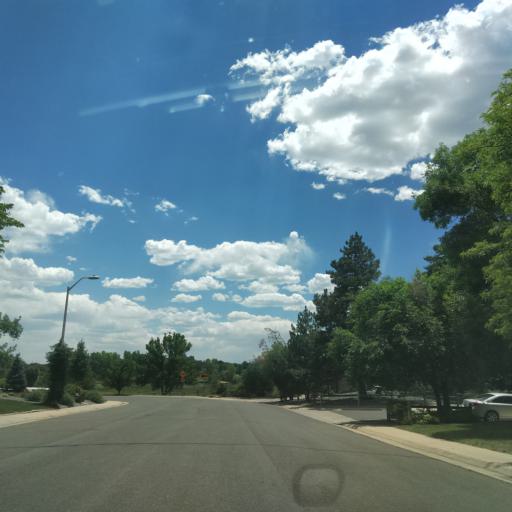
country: US
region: Colorado
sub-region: Jefferson County
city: Lakewood
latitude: 39.6864
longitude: -105.1055
